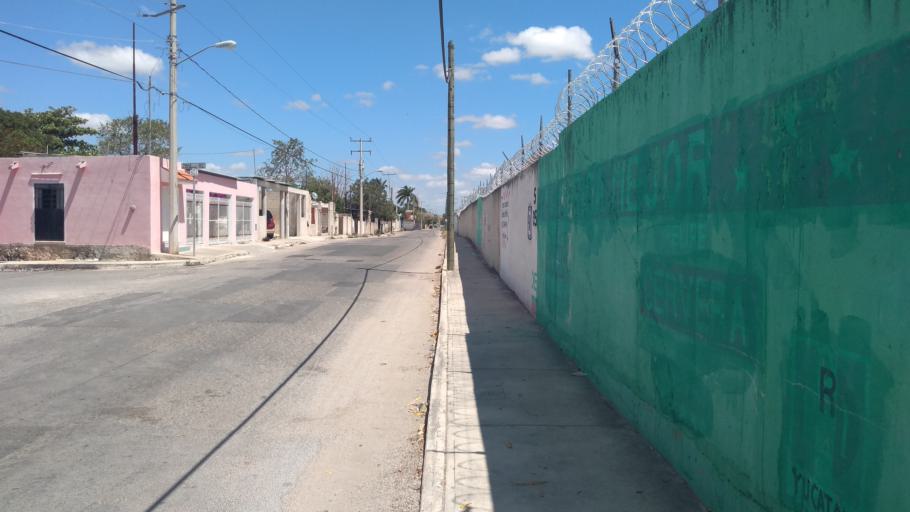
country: MX
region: Yucatan
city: Itzincab Palomeque
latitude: 20.9269
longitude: -89.6660
